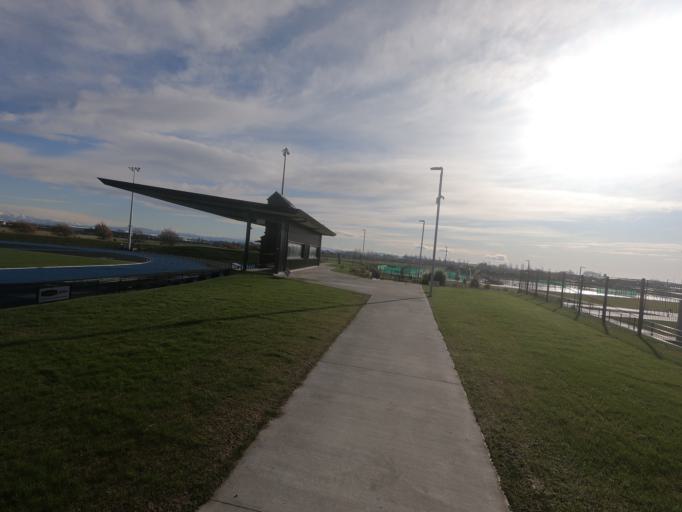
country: NZ
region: Canterbury
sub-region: Selwyn District
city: Prebbleton
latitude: -43.5582
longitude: 172.5748
